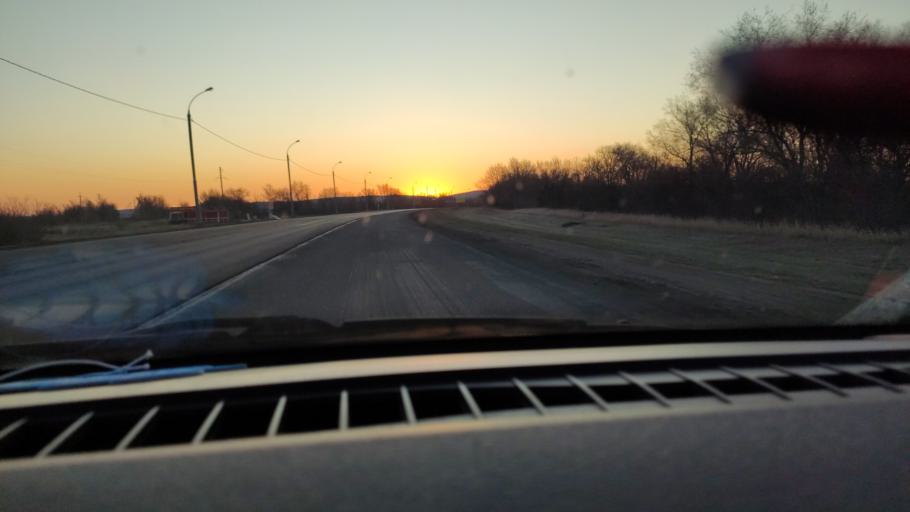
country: RU
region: Saratov
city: Yelshanka
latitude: 51.8297
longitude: 46.2289
